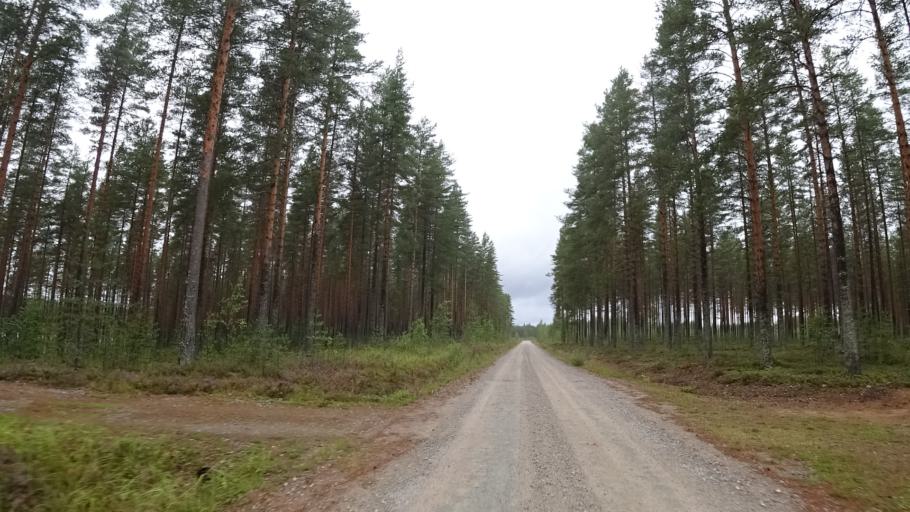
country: FI
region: North Karelia
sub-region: Pielisen Karjala
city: Lieksa
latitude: 63.5308
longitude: 30.0630
